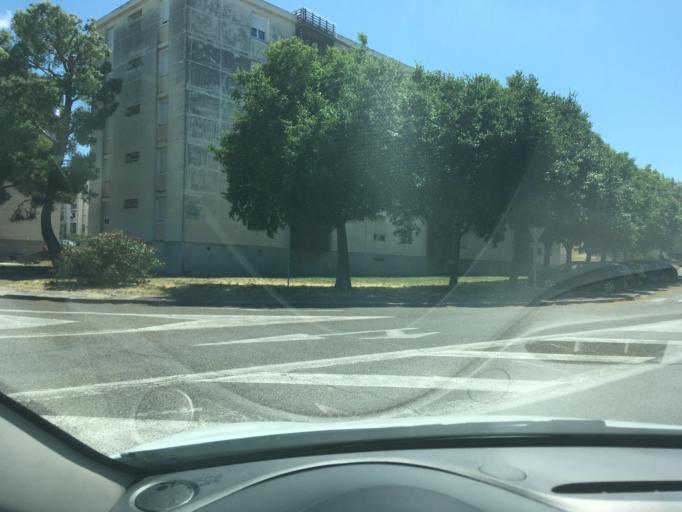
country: FR
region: Provence-Alpes-Cote d'Azur
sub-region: Departement des Bouches-du-Rhone
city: Chateaurenard
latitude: 43.8806
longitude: 4.8666
